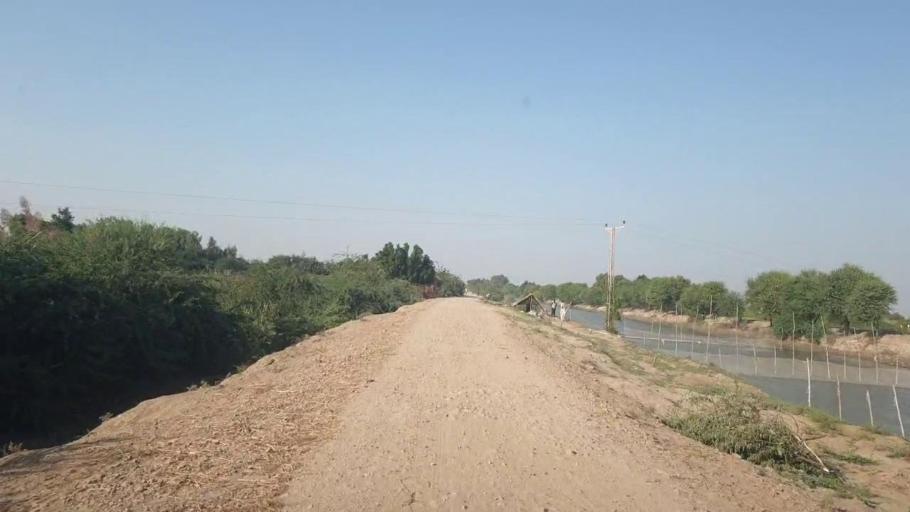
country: PK
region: Sindh
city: Badin
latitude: 24.6475
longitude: 68.8151
